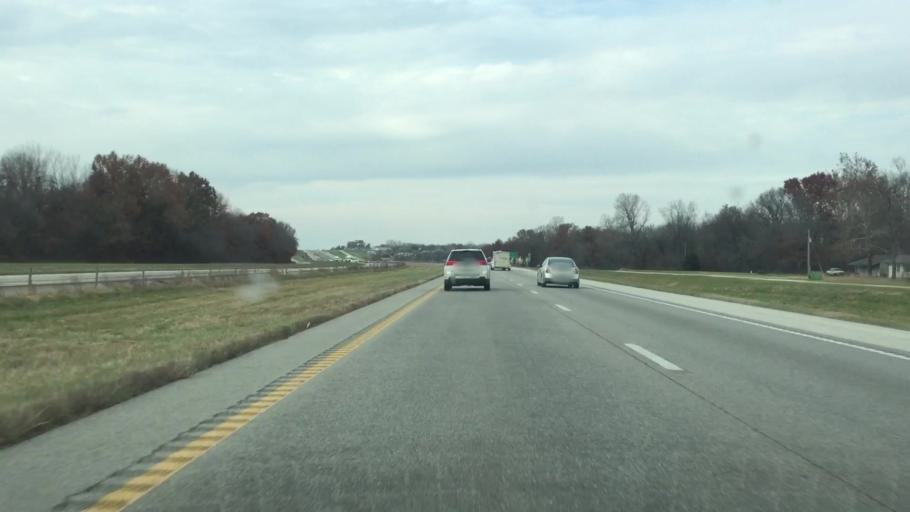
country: US
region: Missouri
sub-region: Cass County
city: Peculiar
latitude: 38.6952
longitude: -94.4296
